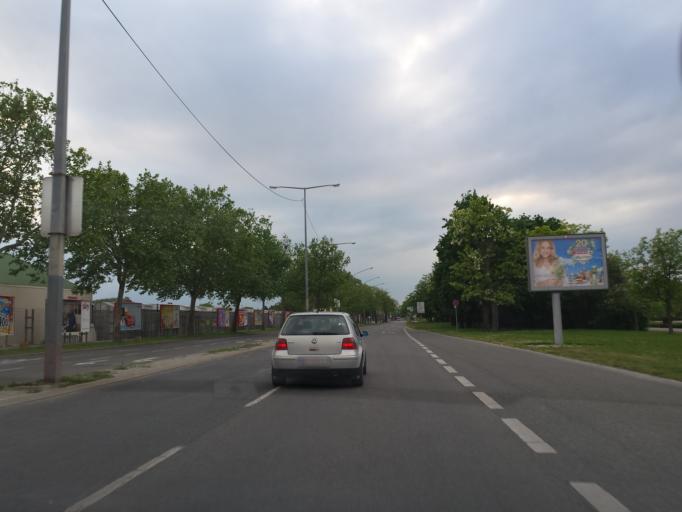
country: AT
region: Lower Austria
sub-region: Politischer Bezirk Ganserndorf
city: Gross-Enzersdorf
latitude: 48.2159
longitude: 16.5035
